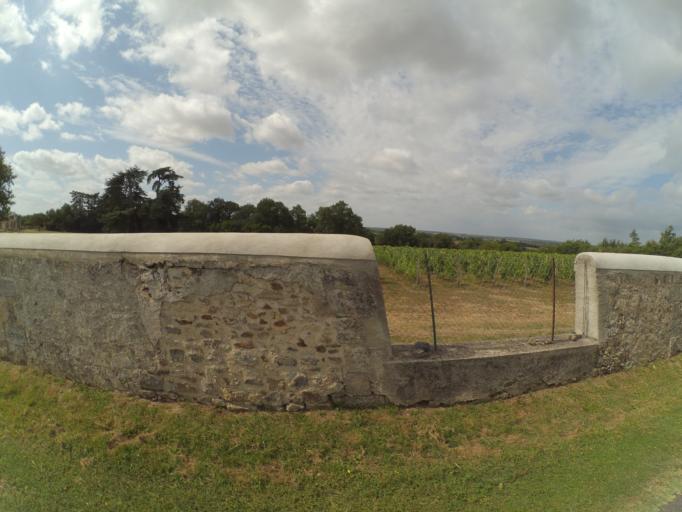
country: FR
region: Pays de la Loire
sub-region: Departement de Maine-et-Loire
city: Saint-Jean
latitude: 47.1910
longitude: -0.3596
